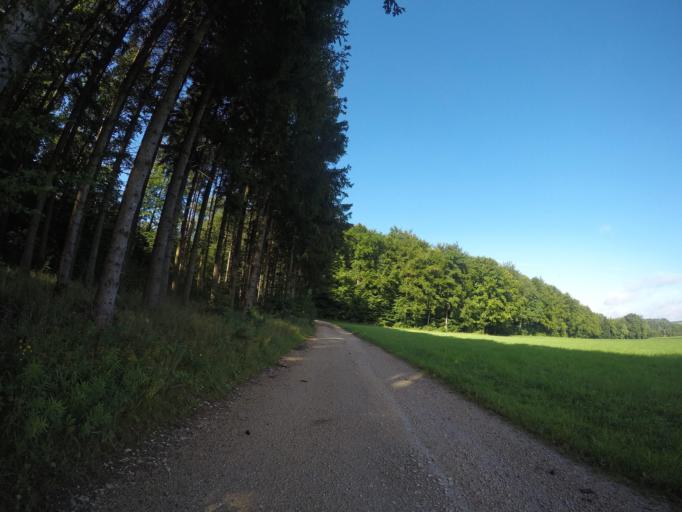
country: DE
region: Baden-Wuerttemberg
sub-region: Tuebingen Region
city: Schelklingen
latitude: 48.3946
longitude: 9.6868
